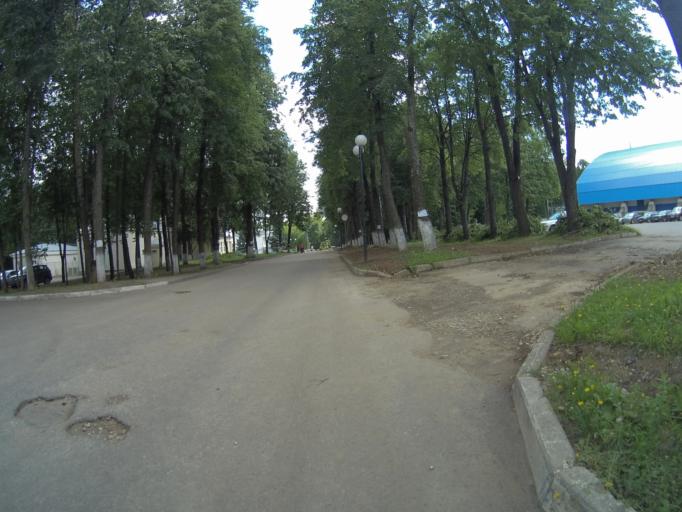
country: RU
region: Vladimir
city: Vladimir
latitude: 56.1432
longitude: 40.4133
